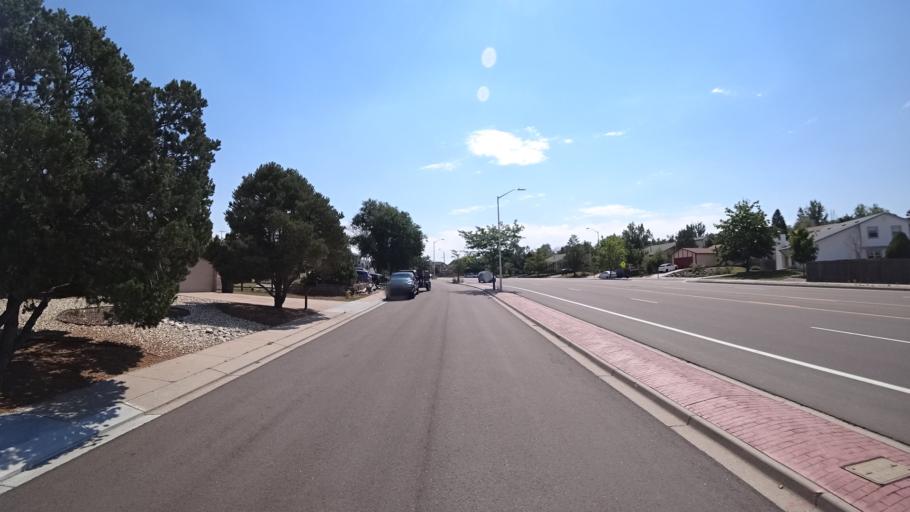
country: US
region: Colorado
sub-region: El Paso County
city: Cimarron Hills
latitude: 38.9252
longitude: -104.7693
